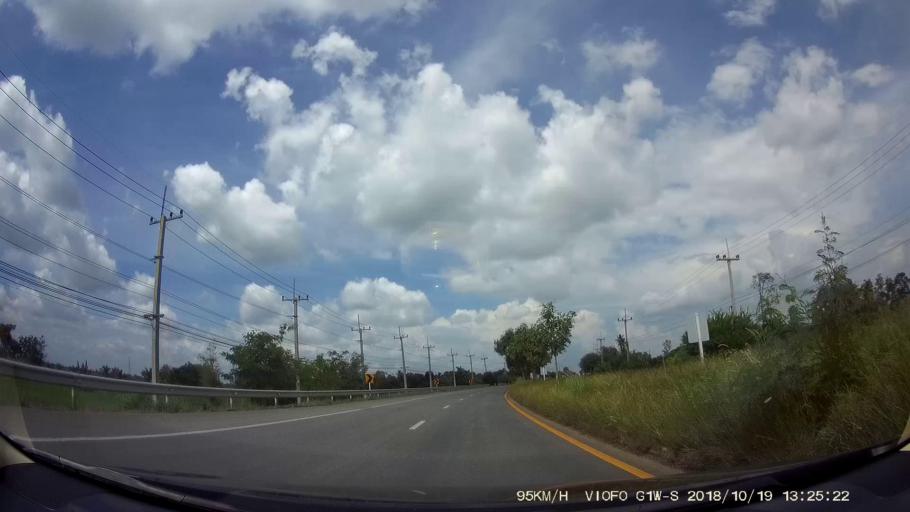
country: TH
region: Chaiyaphum
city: Chatturat
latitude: 15.5203
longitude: 101.8255
